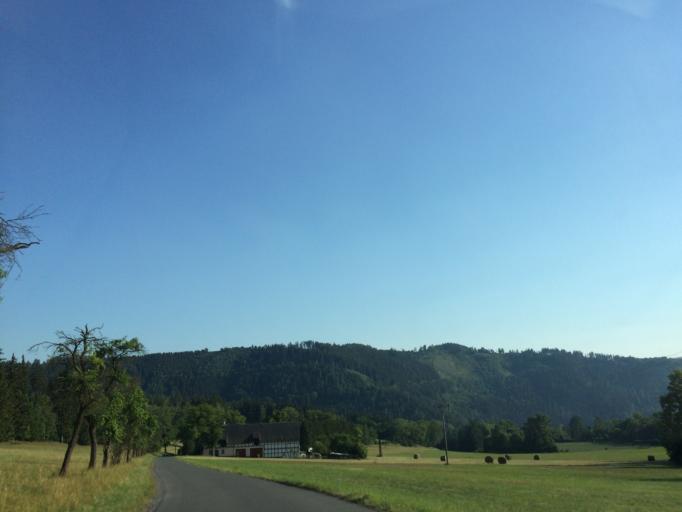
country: DE
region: Thuringia
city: Altenbeuthen
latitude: 50.6072
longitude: 11.5963
